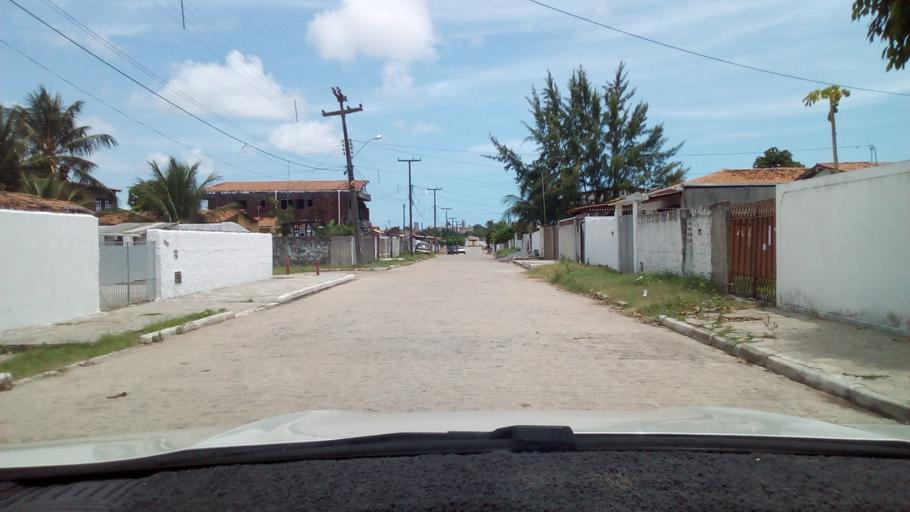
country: BR
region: Paraiba
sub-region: Joao Pessoa
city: Joao Pessoa
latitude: -7.1804
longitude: -34.8282
